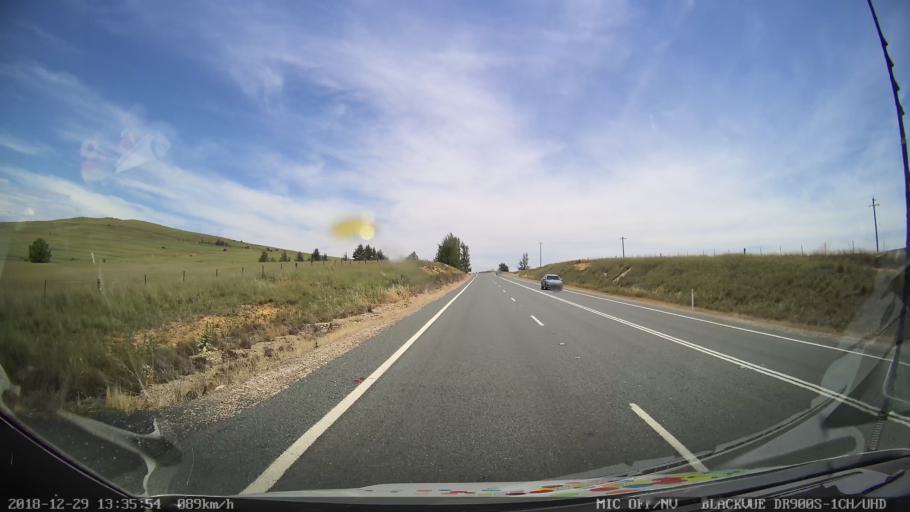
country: AU
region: New South Wales
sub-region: Cooma-Monaro
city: Cooma
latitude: -35.9650
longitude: 149.1463
